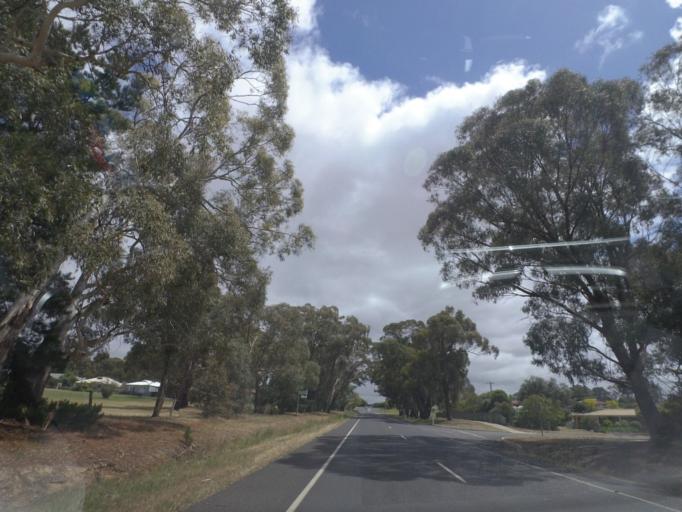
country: AU
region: Victoria
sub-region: Whittlesea
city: Whittlesea
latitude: -37.2118
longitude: 145.0477
